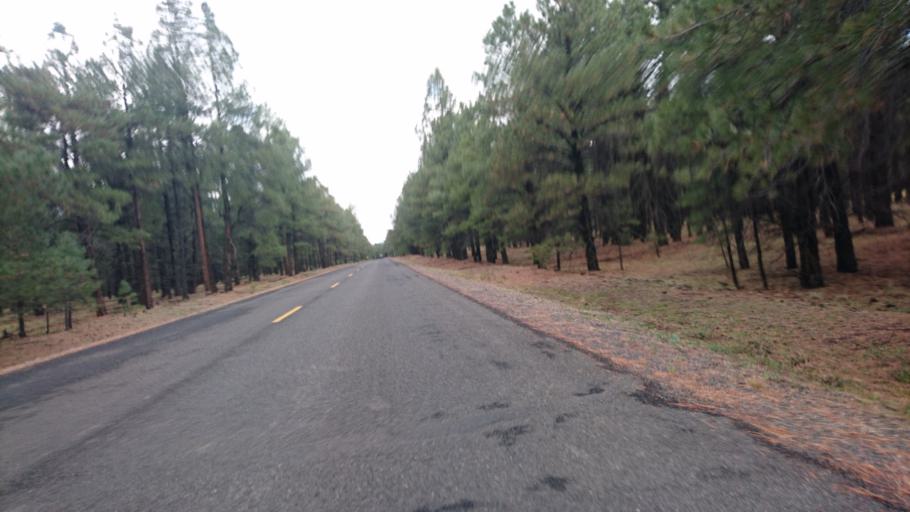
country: US
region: Arizona
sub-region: Coconino County
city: Parks
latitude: 35.2596
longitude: -111.8696
